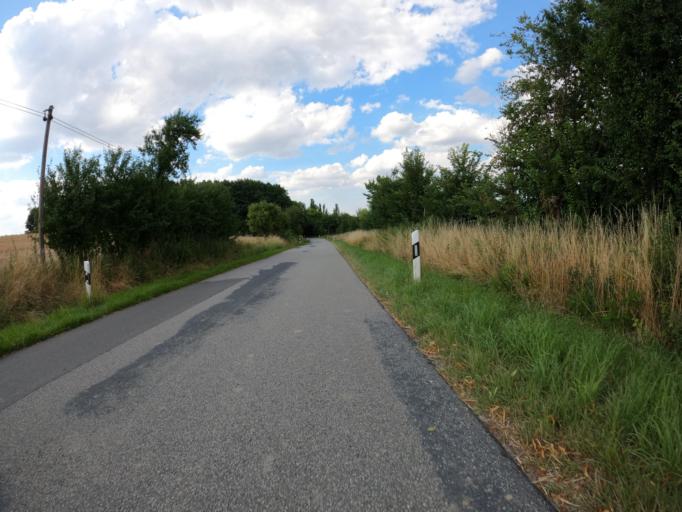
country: DE
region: Mecklenburg-Vorpommern
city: Woldegk
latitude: 53.4483
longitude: 13.5849
